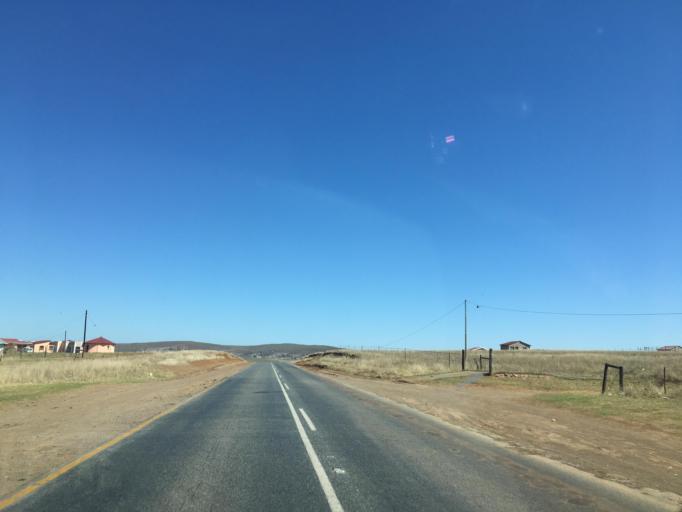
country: ZA
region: Eastern Cape
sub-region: Chris Hani District Municipality
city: Cofimvaba
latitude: -31.9571
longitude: 27.8253
